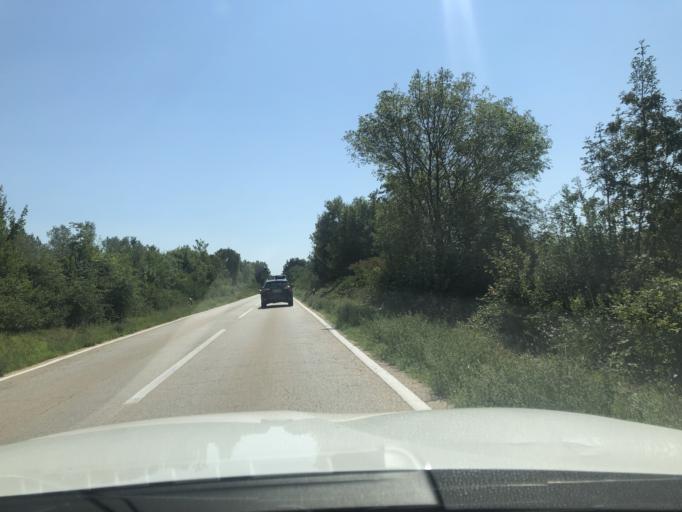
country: HR
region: Istarska
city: Vodnjan
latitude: 45.0237
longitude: 13.8006
